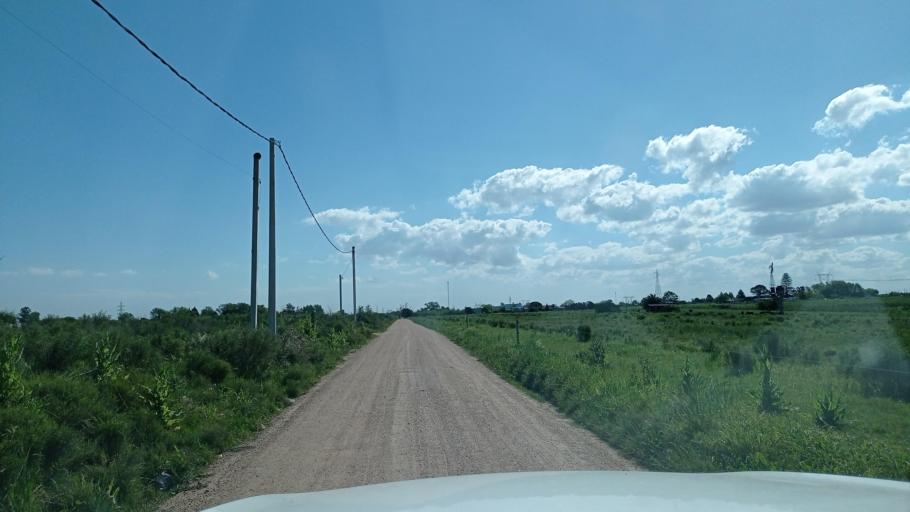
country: UY
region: Canelones
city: La Paz
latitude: -34.7824
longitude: -56.1598
